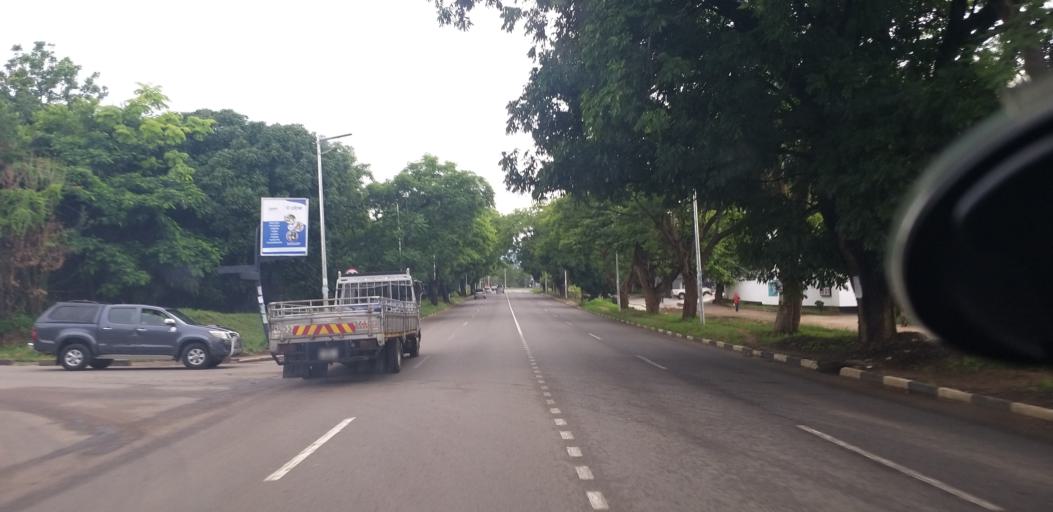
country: ZM
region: Lusaka
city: Lusaka
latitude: -15.4152
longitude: 28.2936
